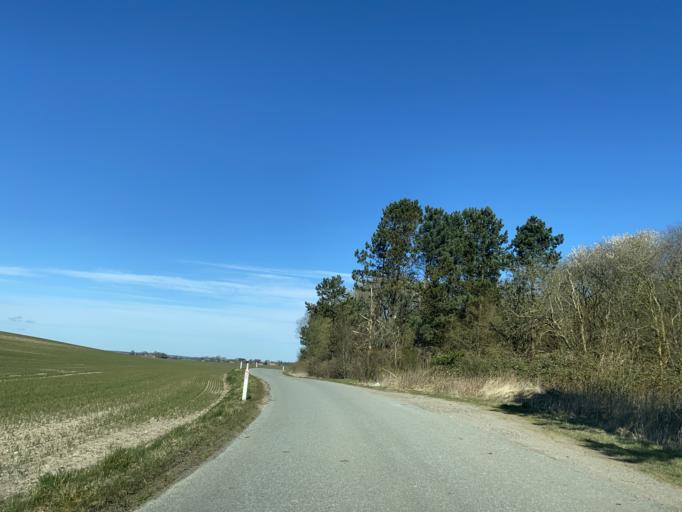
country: DK
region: Central Jutland
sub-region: Randers Kommune
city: Langa
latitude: 56.3843
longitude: 9.9568
